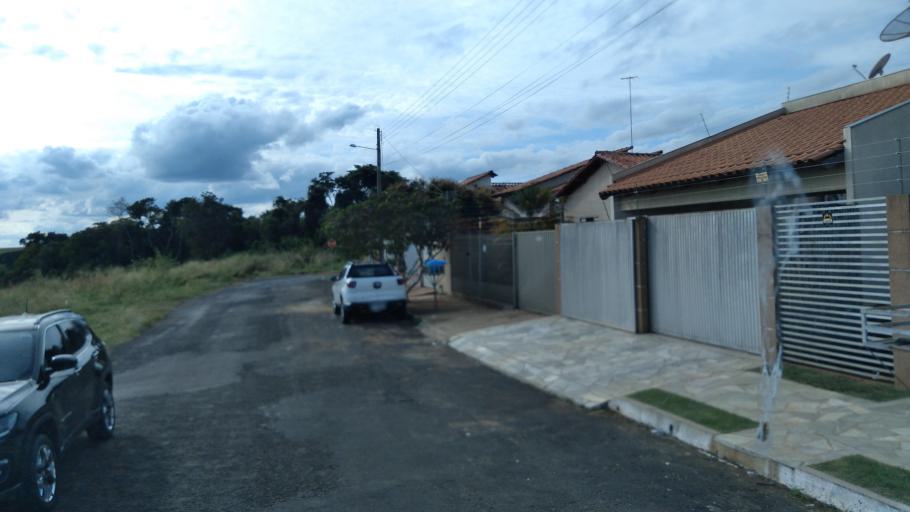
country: BR
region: Goias
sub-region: Mineiros
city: Mineiros
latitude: -17.5607
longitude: -52.5674
